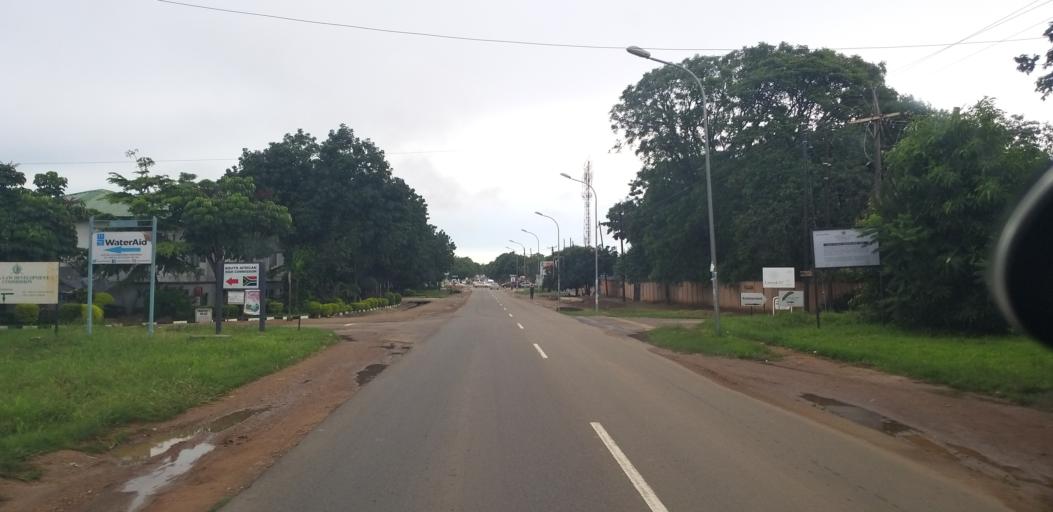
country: ZM
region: Lusaka
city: Lusaka
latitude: -15.4351
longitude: 28.3524
